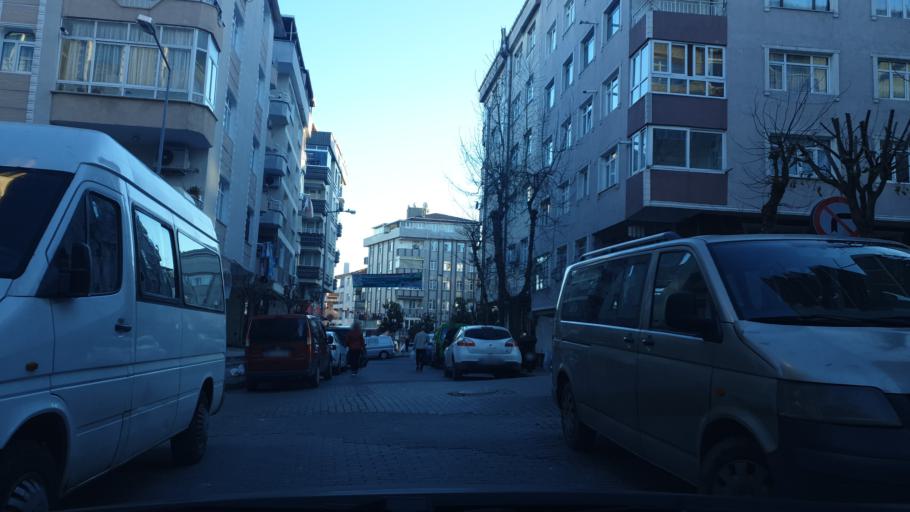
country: TR
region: Istanbul
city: merter keresteciler
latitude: 41.0193
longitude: 28.8756
